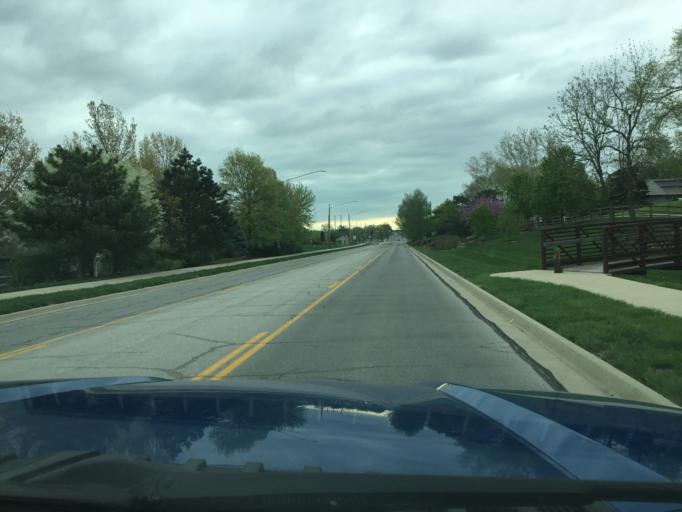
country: US
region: Kansas
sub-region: Douglas County
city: Lawrence
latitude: 38.9861
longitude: -95.2832
